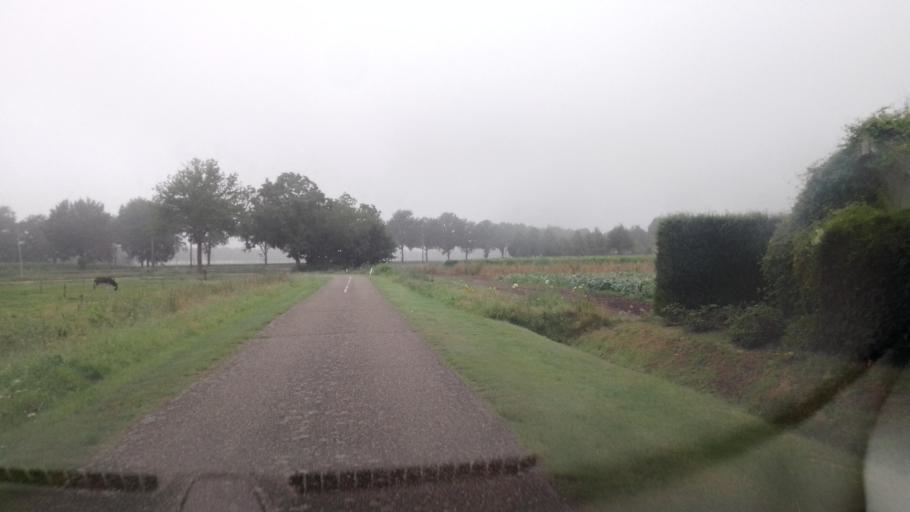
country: NL
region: Limburg
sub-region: Gemeente Peel en Maas
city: Maasbree
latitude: 51.4319
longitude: 6.0249
